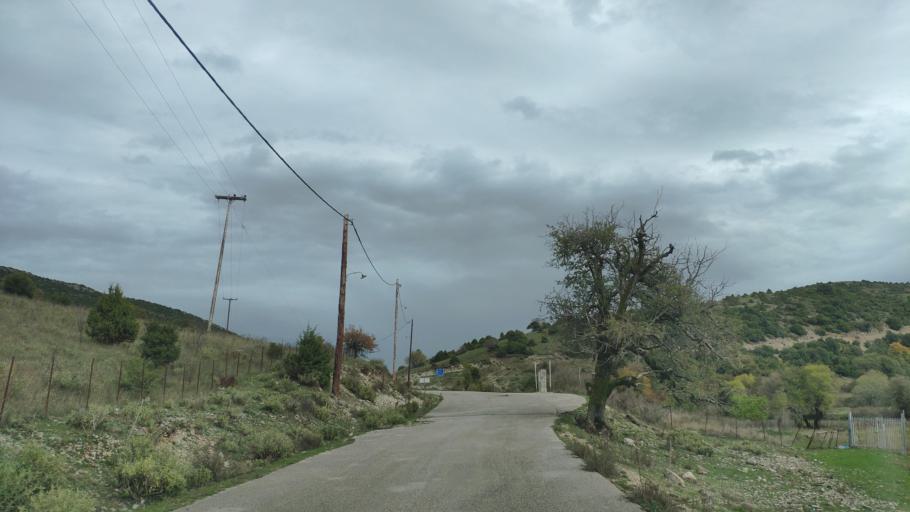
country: GR
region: Epirus
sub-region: Nomos Thesprotias
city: Paramythia
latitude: 39.4490
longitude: 20.6469
